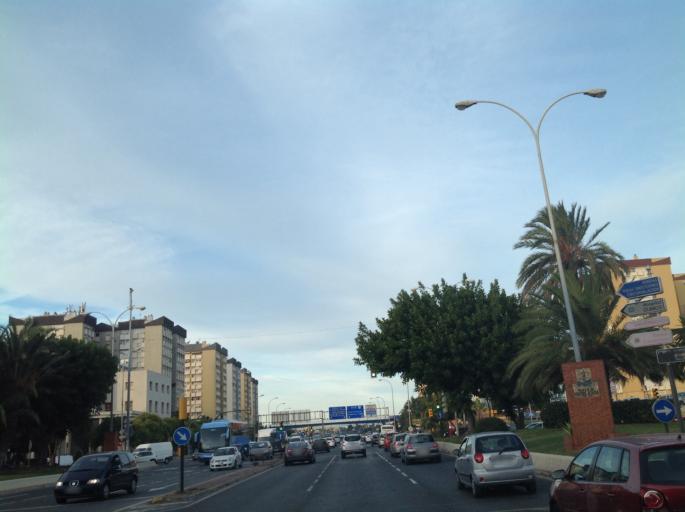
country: ES
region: Andalusia
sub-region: Provincia de Malaga
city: Malaga
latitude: 36.7152
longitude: -4.4478
